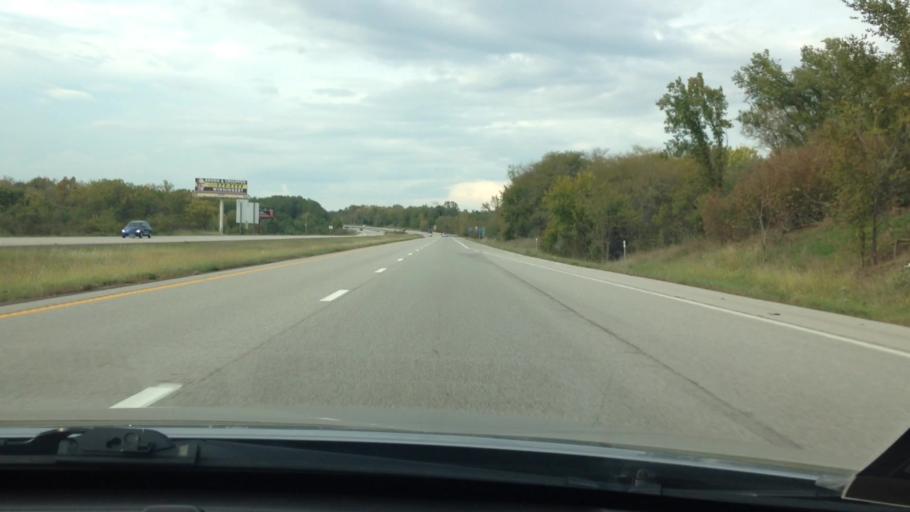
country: US
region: Missouri
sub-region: Platte County
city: Weatherby Lake
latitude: 39.2499
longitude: -94.7549
